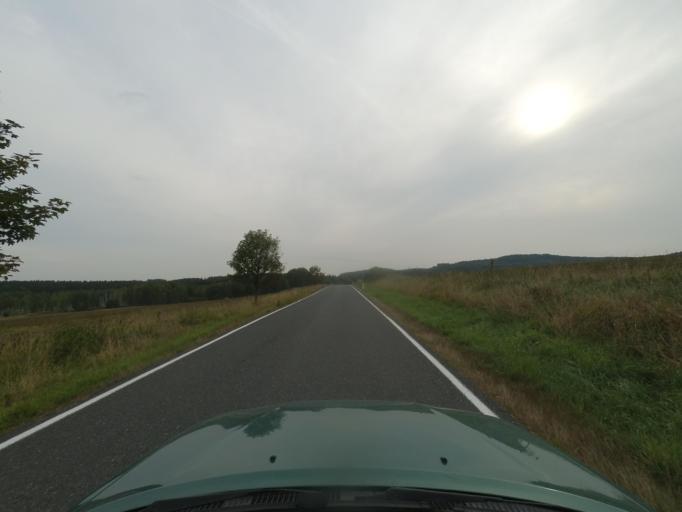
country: DE
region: Bavaria
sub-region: Upper Palatinate
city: Eslarn
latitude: 49.5890
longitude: 12.6060
